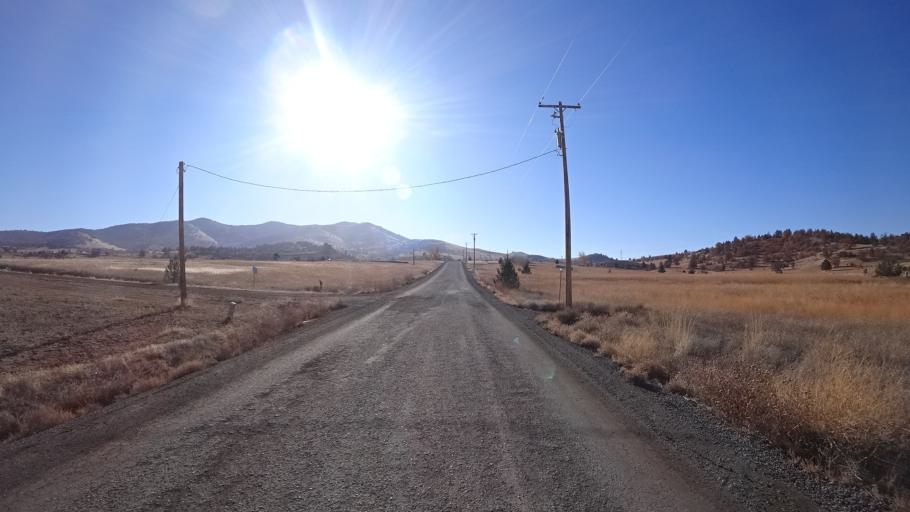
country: US
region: California
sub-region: Siskiyou County
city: Montague
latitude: 41.8807
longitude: -122.4240
